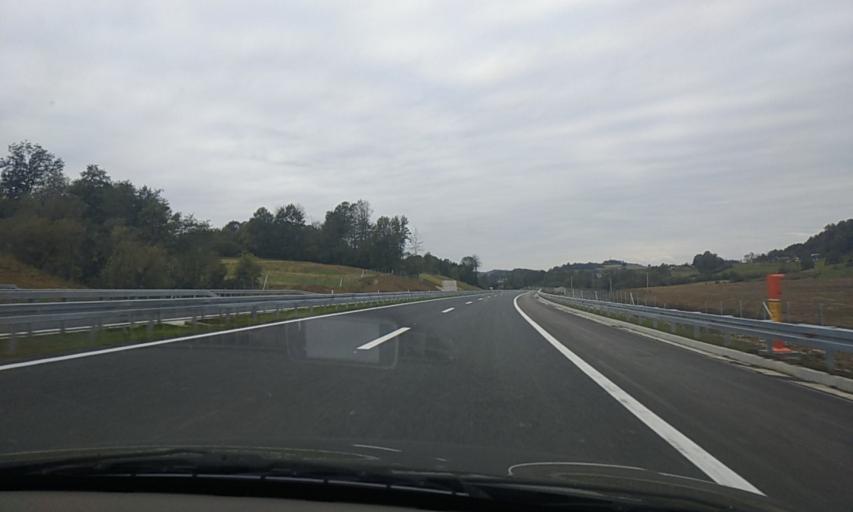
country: BA
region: Republika Srpska
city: Maglajani
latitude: 44.8611
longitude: 17.4820
